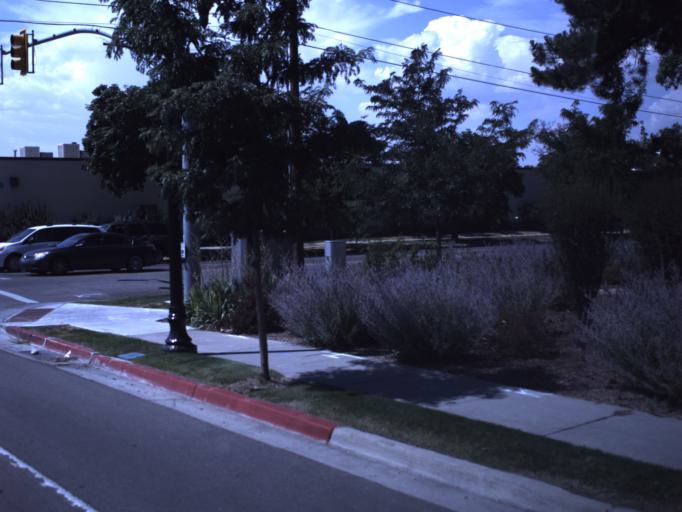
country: US
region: Utah
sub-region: Cache County
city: Logan
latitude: 41.7390
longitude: -111.8292
